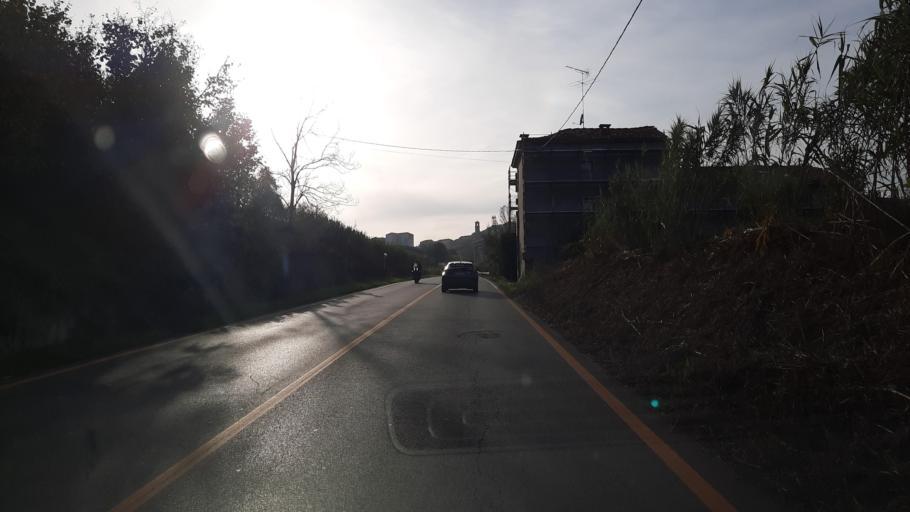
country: IT
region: Piedmont
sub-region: Provincia di Asti
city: Moncalvo
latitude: 45.0538
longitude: 8.2764
